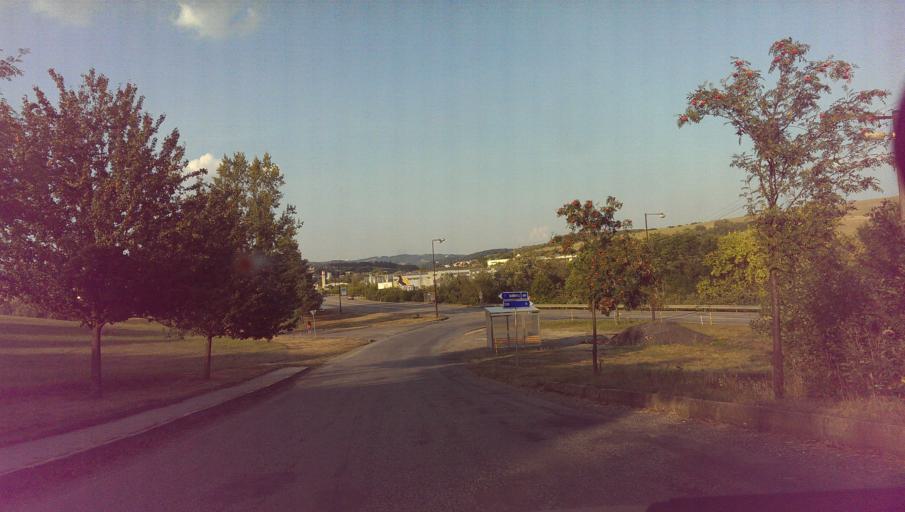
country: CZ
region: Zlin
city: Slusovice
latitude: 49.2379
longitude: 17.7882
